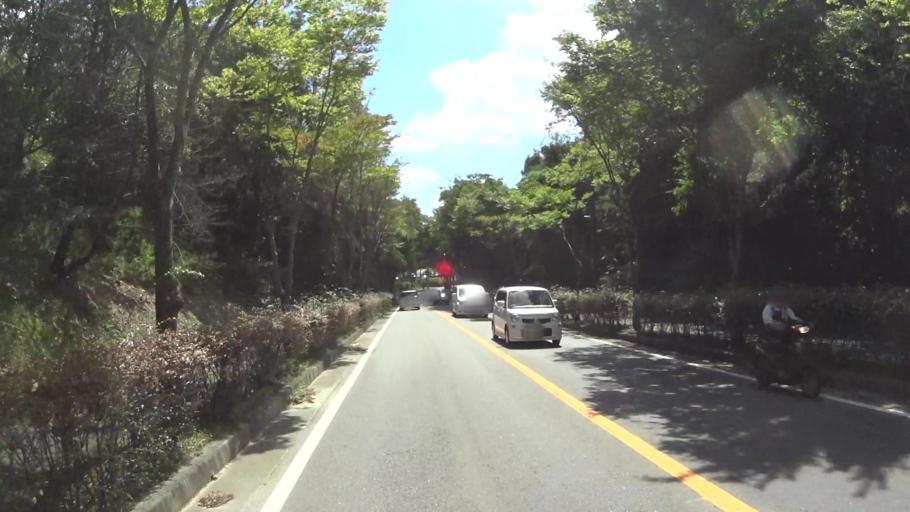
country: JP
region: Kyoto
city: Uji
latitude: 34.8584
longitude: 135.8006
